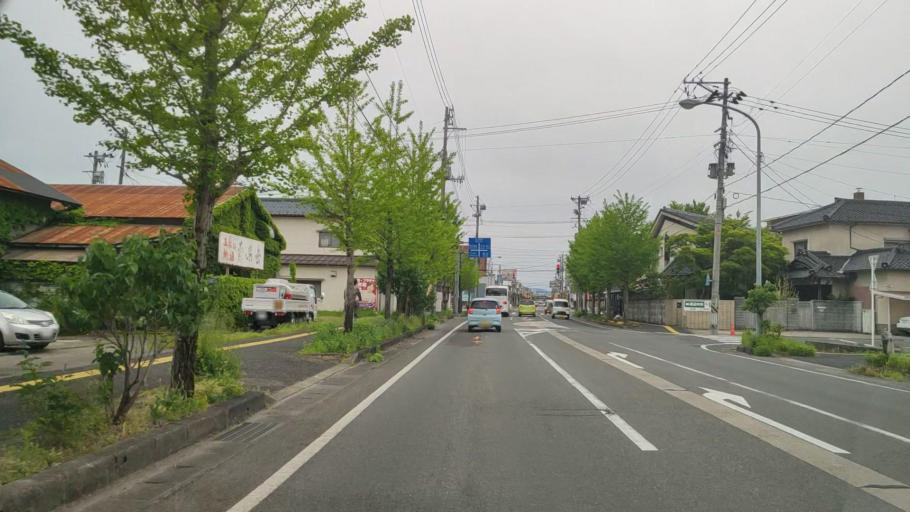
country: JP
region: Niigata
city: Gosen
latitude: 37.7388
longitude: 139.1806
